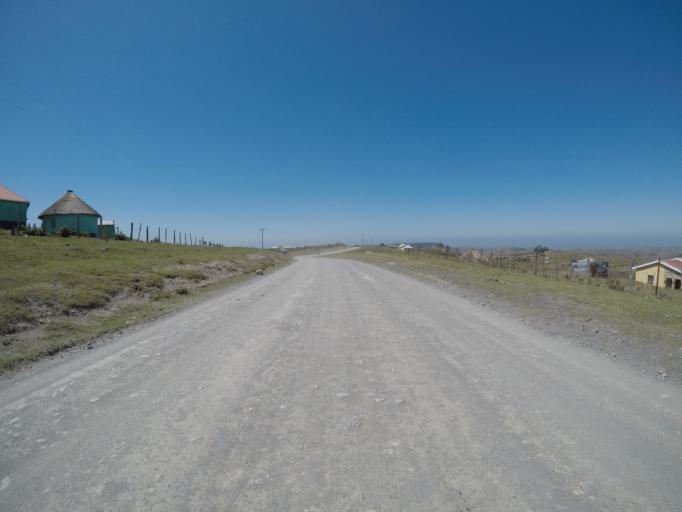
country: ZA
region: Eastern Cape
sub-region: OR Tambo District Municipality
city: Libode
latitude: -31.9835
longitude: 29.0444
